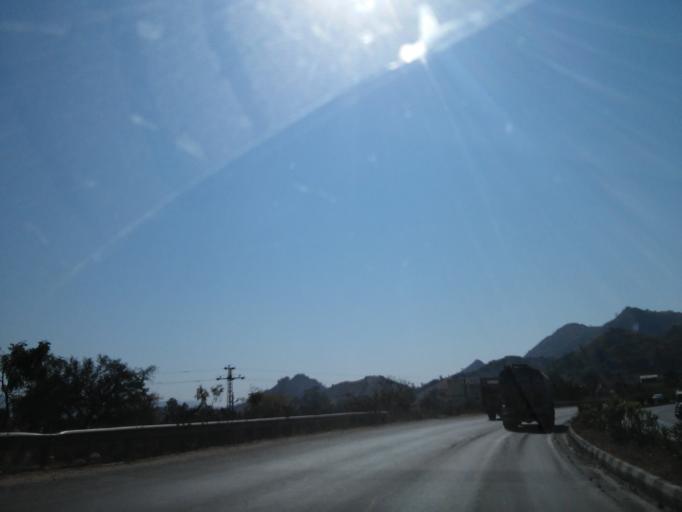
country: IN
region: Rajasthan
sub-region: Dungarpur
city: Dungarpur
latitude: 24.1371
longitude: 73.6952
